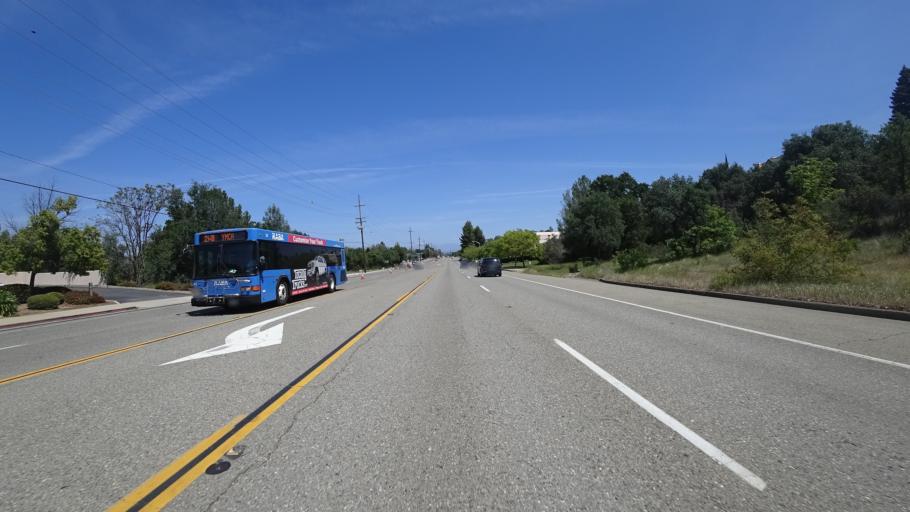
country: US
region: California
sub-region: Shasta County
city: Redding
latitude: 40.5855
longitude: -122.4162
